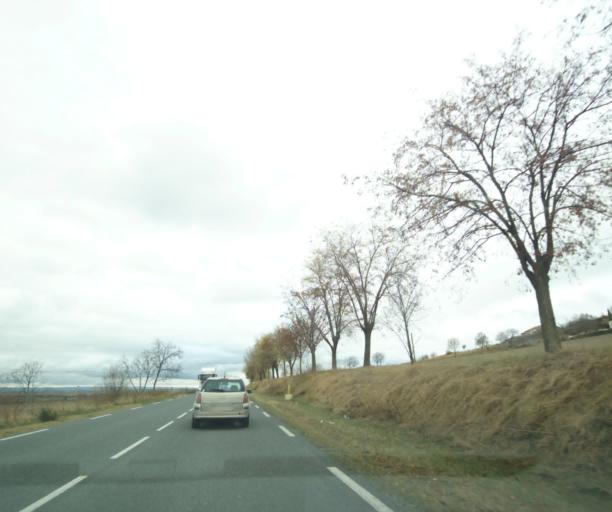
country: FR
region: Auvergne
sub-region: Departement du Puy-de-Dome
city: Pont-du-Chateau
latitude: 45.8009
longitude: 3.2264
